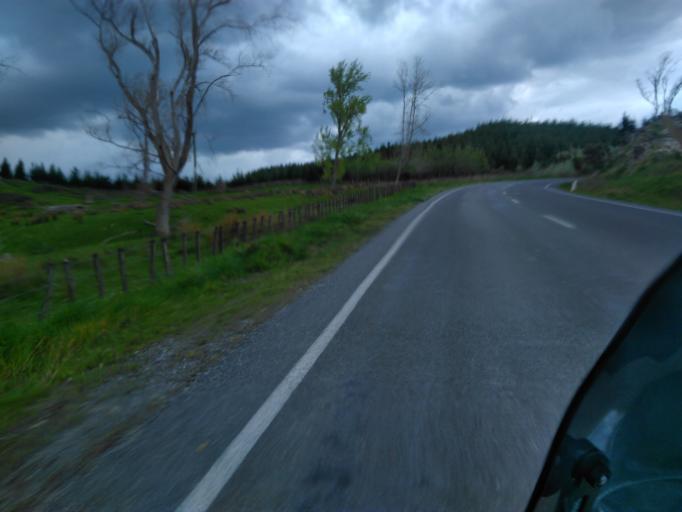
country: NZ
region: Gisborne
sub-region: Gisborne District
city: Gisborne
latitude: -38.6789
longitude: 177.8019
